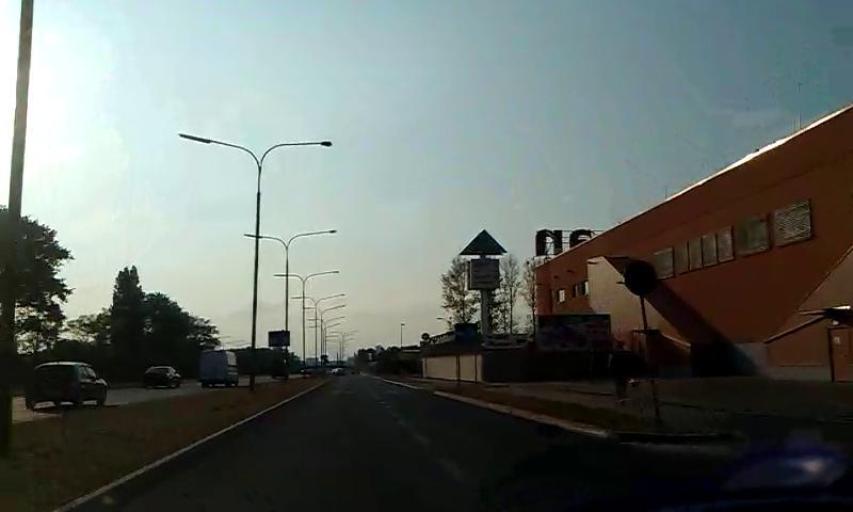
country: PL
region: Lublin Voivodeship
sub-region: Powiat lubelski
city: Jakubowice Murowane
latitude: 51.2311
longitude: 22.6114
